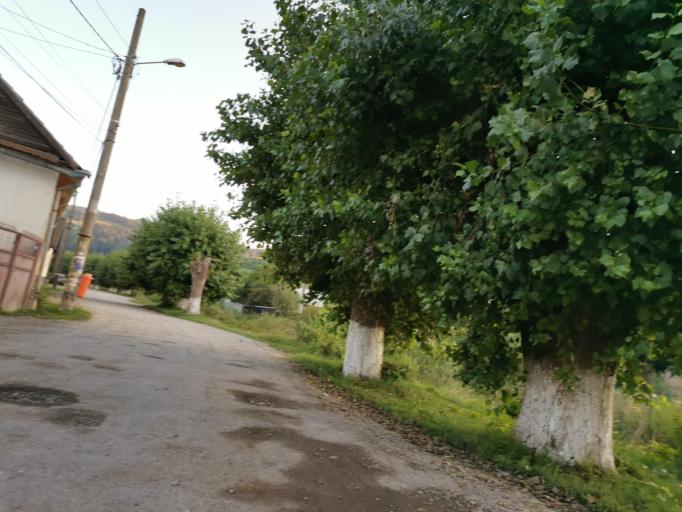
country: RO
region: Brasov
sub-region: Comuna Tarlungeni
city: Zizin
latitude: 45.6369
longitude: 25.7745
